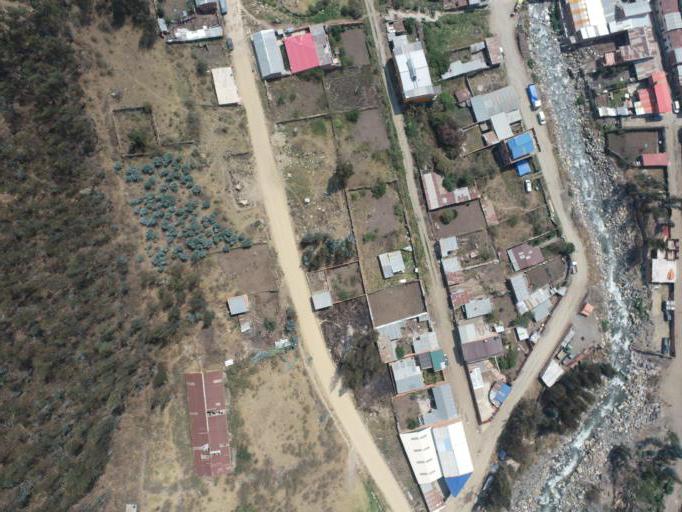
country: BO
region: La Paz
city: Quime
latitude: -16.9783
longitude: -67.2174
